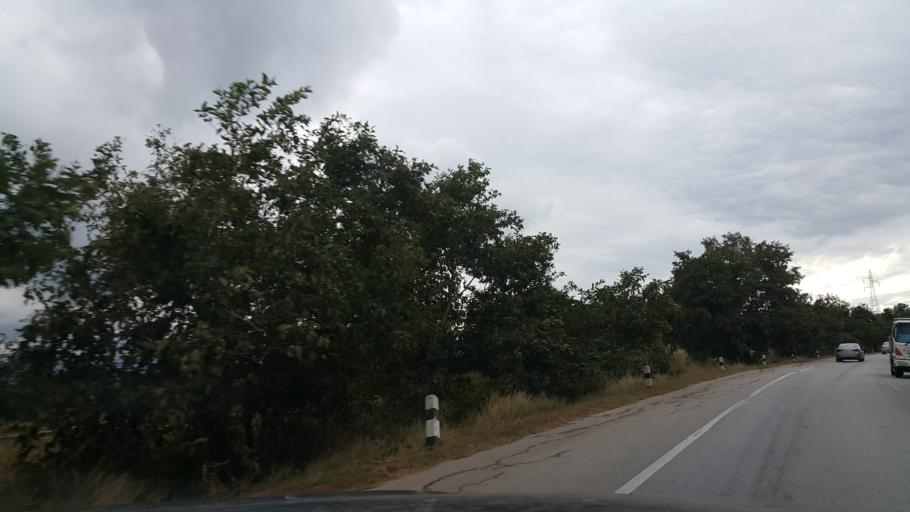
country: TH
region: Lampang
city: Sop Prap
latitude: 17.9587
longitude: 99.3545
